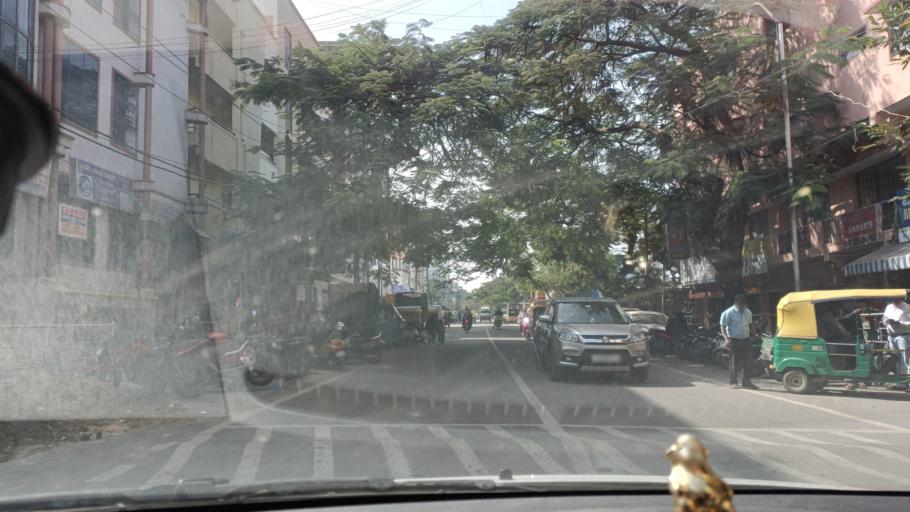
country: IN
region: Karnataka
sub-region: Bangalore Urban
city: Bangalore
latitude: 12.9195
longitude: 77.6150
